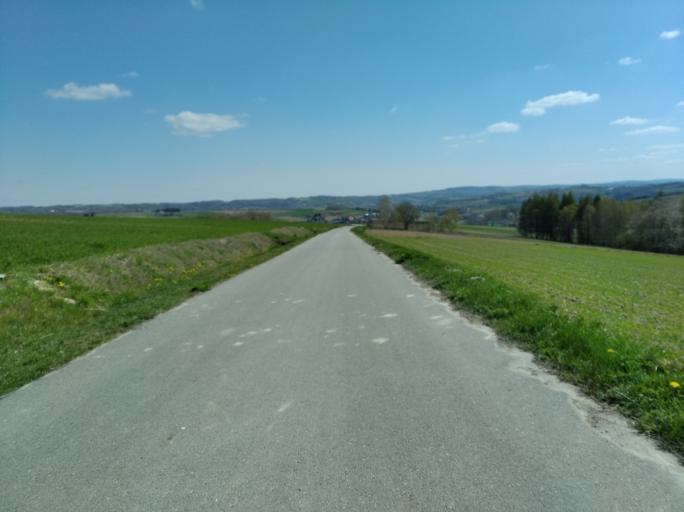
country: PL
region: Subcarpathian Voivodeship
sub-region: Powiat strzyzowski
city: Wisniowa
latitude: 49.9093
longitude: 21.6574
